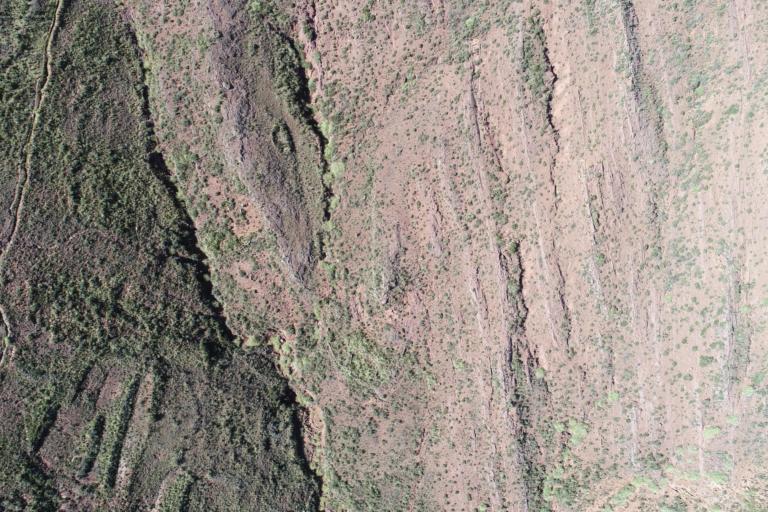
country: BO
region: La Paz
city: Tiahuanaco
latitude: -16.6048
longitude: -68.7580
